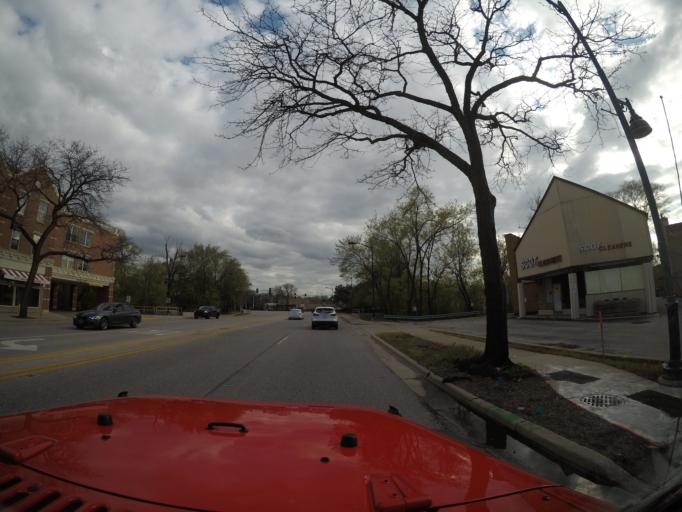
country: US
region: Illinois
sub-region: Cook County
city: Glenview
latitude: 42.0724
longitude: -87.7992
